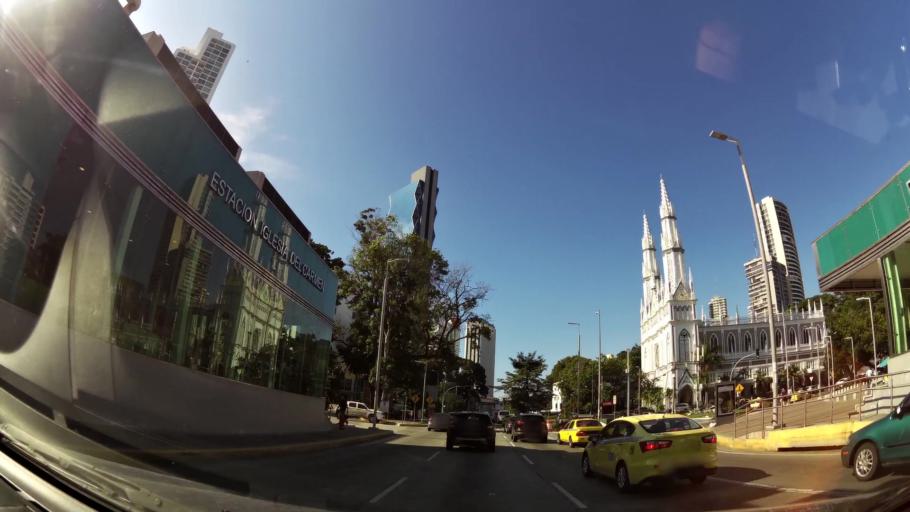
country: PA
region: Panama
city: Panama
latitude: 8.9819
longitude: -79.5274
